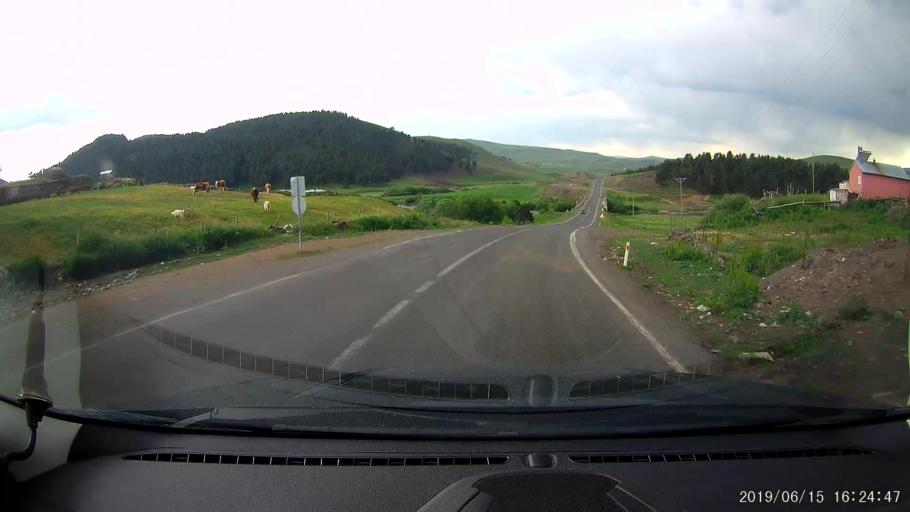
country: TR
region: Ardahan
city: Hanak
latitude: 41.1617
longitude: 42.8724
